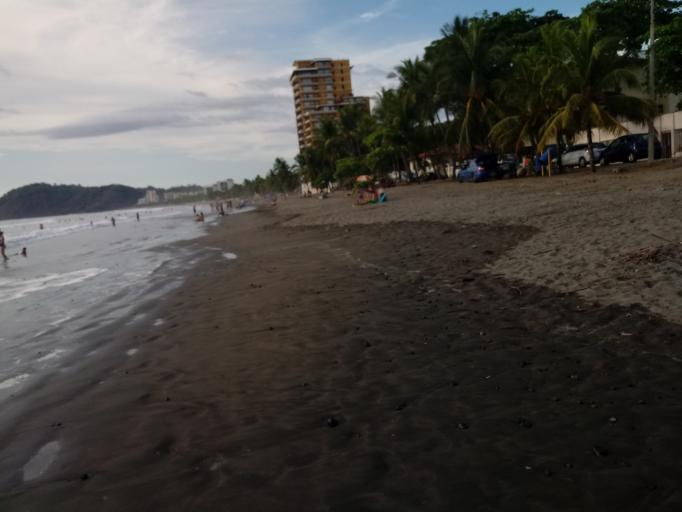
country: CR
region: Puntarenas
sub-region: Canton de Garabito
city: Jaco
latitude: 9.6083
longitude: -84.6256
